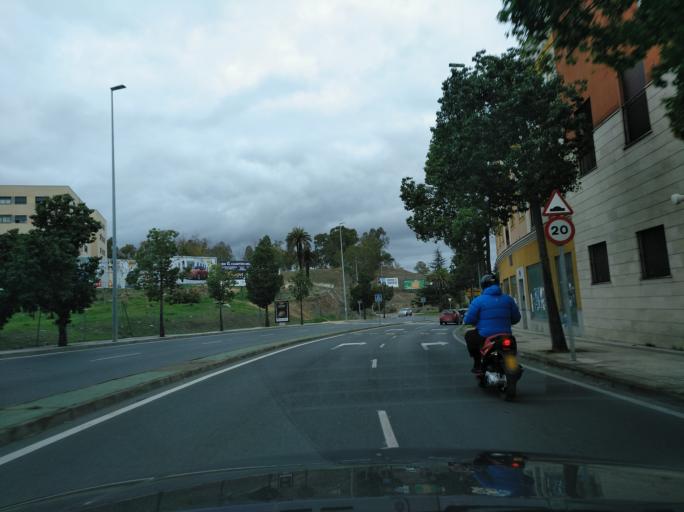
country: ES
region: Extremadura
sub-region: Provincia de Badajoz
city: Badajoz
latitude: 38.8863
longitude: -6.9767
